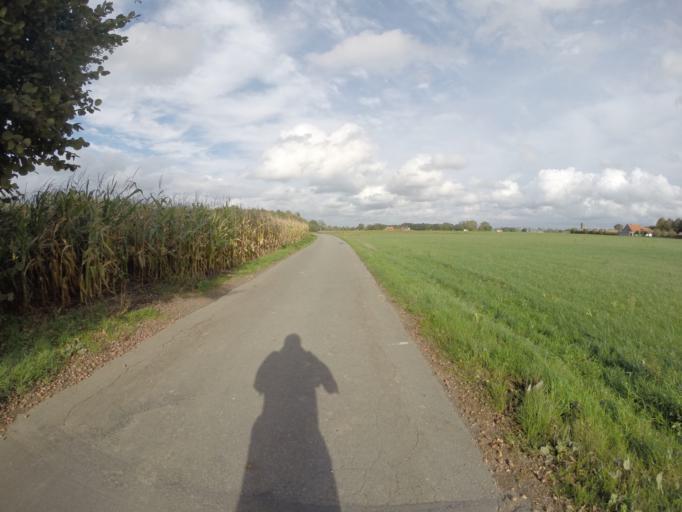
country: BE
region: Flanders
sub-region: Provincie Oost-Vlaanderen
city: Aalter
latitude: 51.0785
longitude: 3.4101
